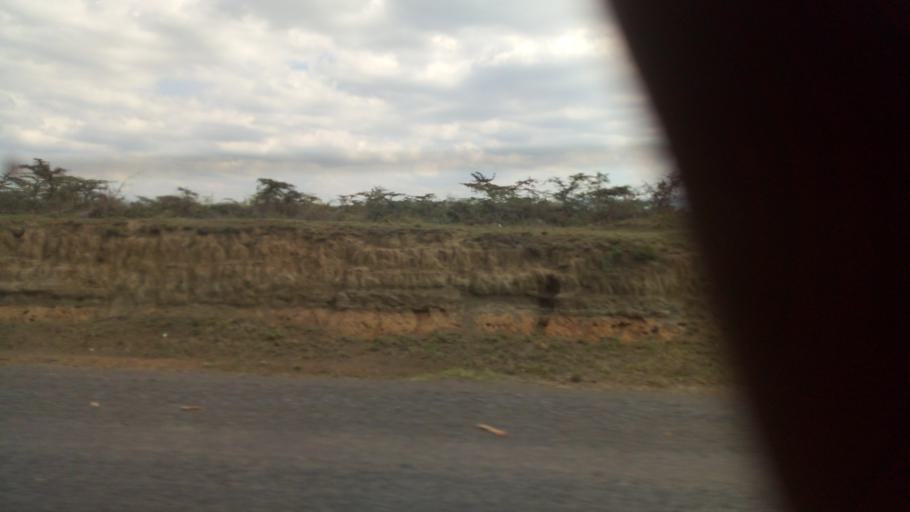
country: KE
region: Nakuru
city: Kijabe
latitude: -1.0163
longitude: 36.4792
